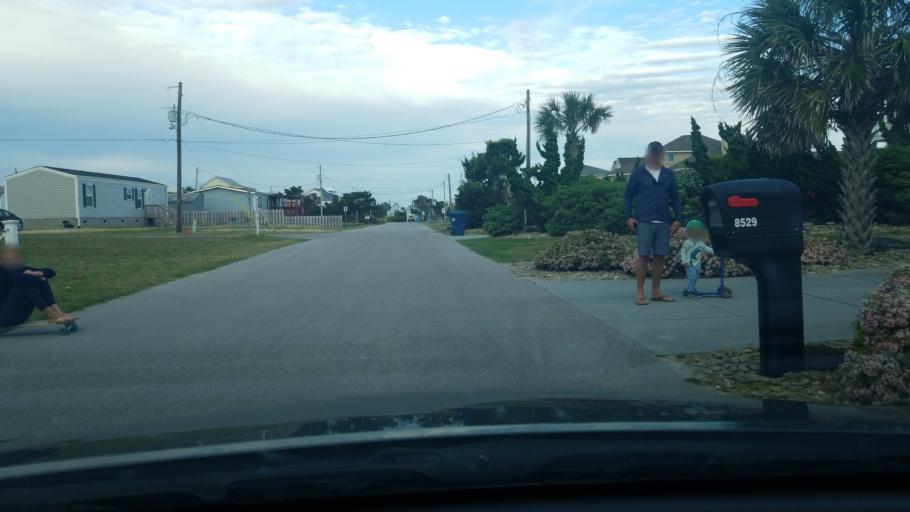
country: US
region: North Carolina
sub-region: Carteret County
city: Cape Carteret
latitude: 34.6597
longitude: -77.0409
